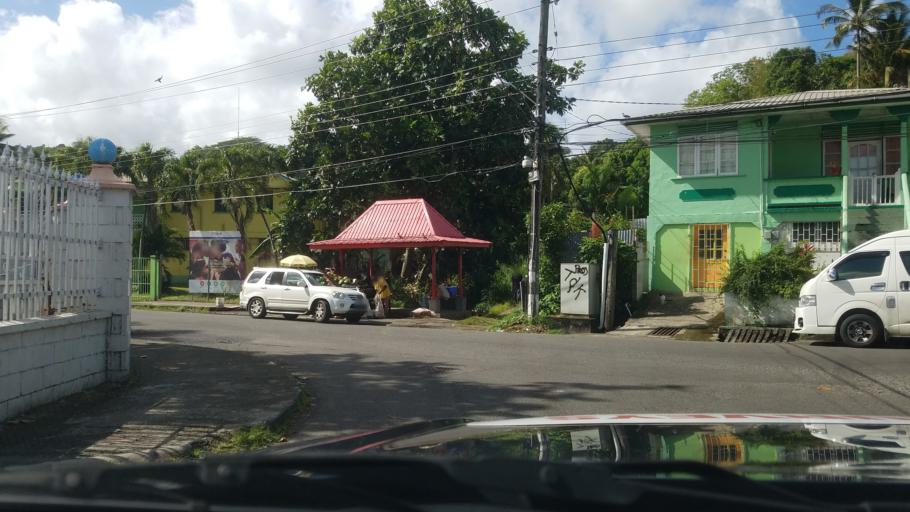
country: LC
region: Castries Quarter
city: Bisee
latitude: 14.0184
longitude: -60.9836
